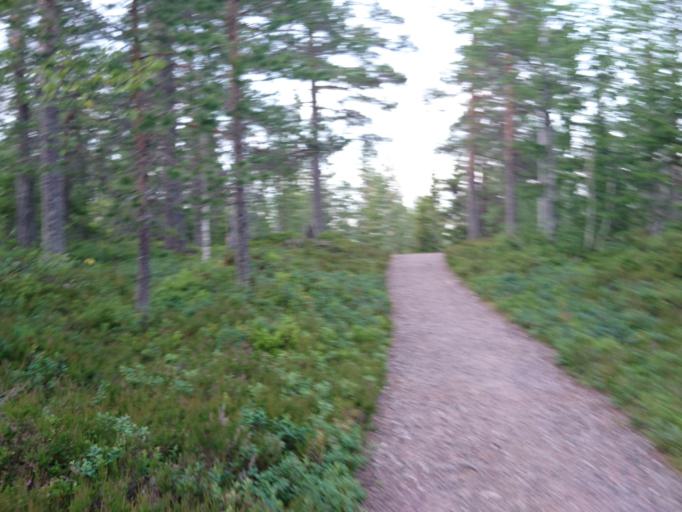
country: SE
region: Dalarna
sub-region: Malung-Saelens kommun
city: Malung
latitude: 61.1704
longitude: 13.1814
